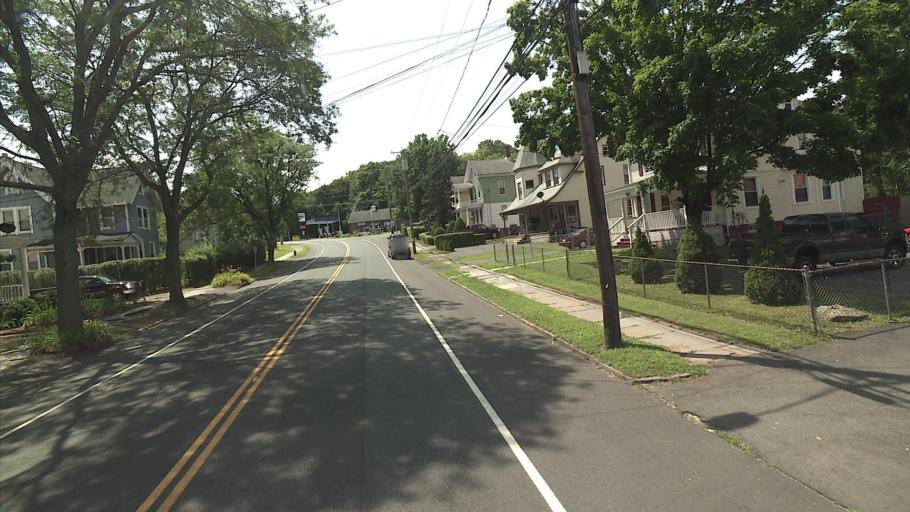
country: US
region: Connecticut
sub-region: New Haven County
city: Meriden
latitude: 41.5289
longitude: -72.8088
